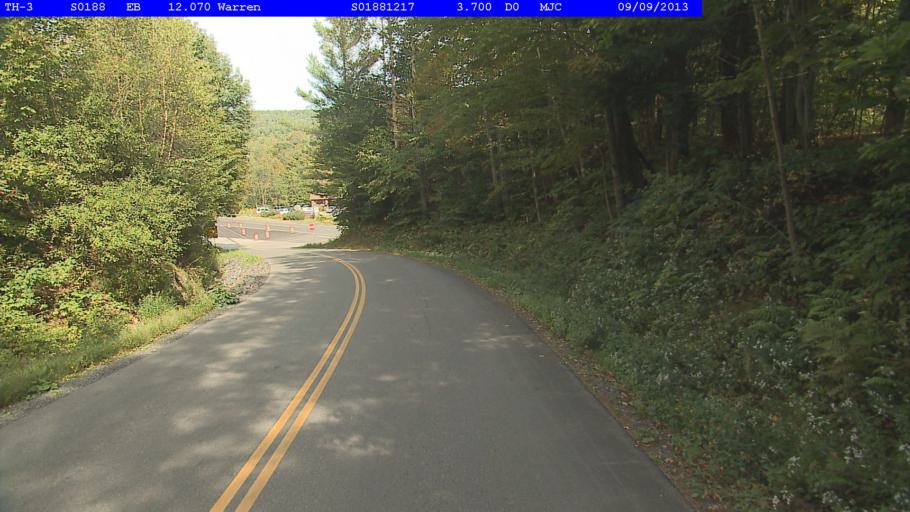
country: US
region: Vermont
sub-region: Washington County
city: Northfield
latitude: 44.1074
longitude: -72.8604
